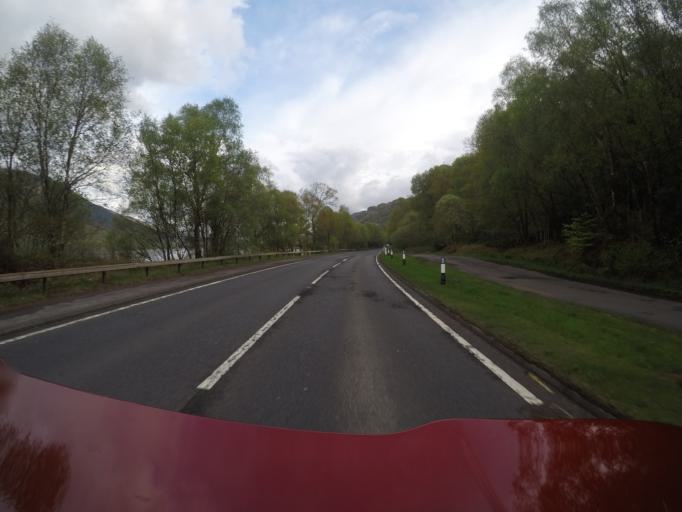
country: GB
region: Scotland
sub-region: Argyll and Bute
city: Garelochhead
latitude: 56.1934
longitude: -4.7004
